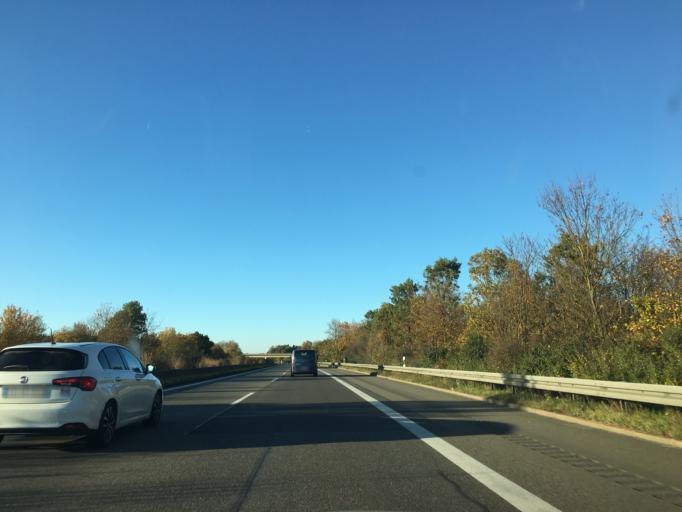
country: DE
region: Baden-Wuerttemberg
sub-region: Freiburg Region
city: Deisslingen
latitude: 48.1161
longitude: 8.5807
